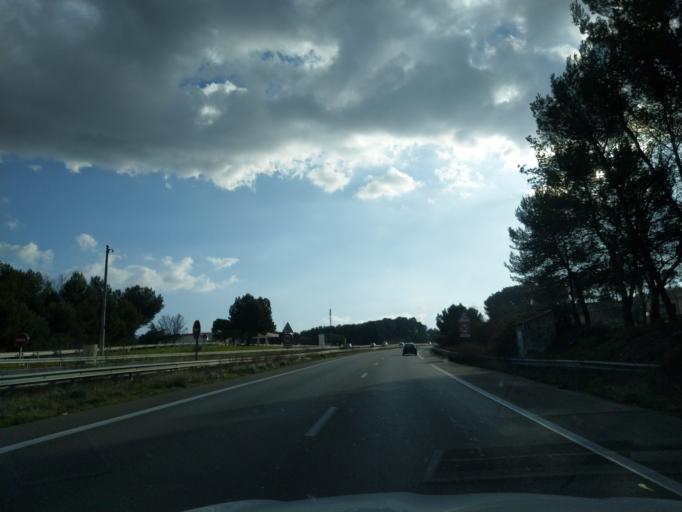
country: FR
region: Provence-Alpes-Cote d'Azur
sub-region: Departement des Bouches-du-Rhone
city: Cabries
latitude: 43.4357
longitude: 5.3956
